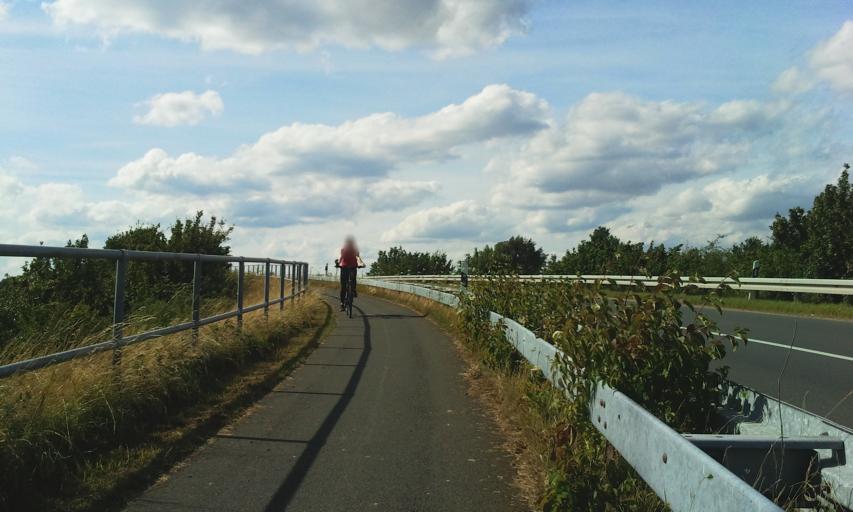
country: DE
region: Lower Saxony
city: Drakenburg
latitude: 52.6808
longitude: 9.2231
